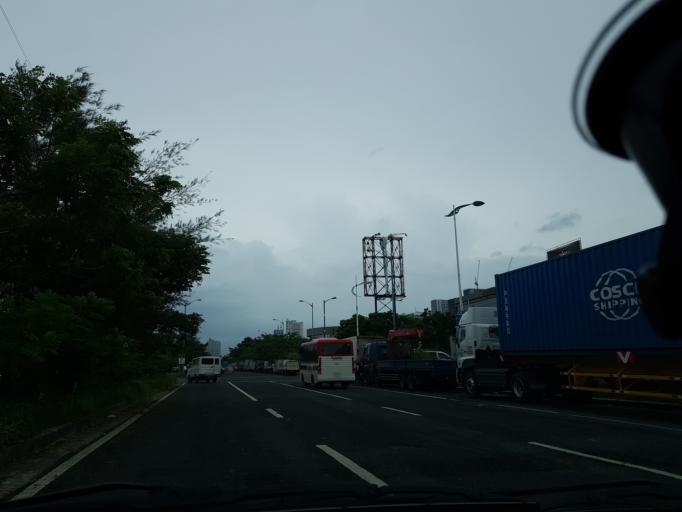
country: PH
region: Metro Manila
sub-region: City of Manila
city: Port Area
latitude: 14.5459
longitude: 120.9875
